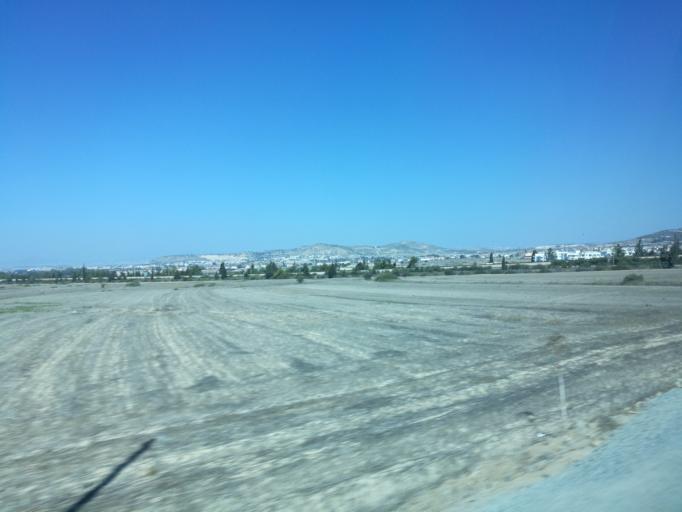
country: CY
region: Larnaka
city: Pyla
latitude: 34.9893
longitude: 33.6968
